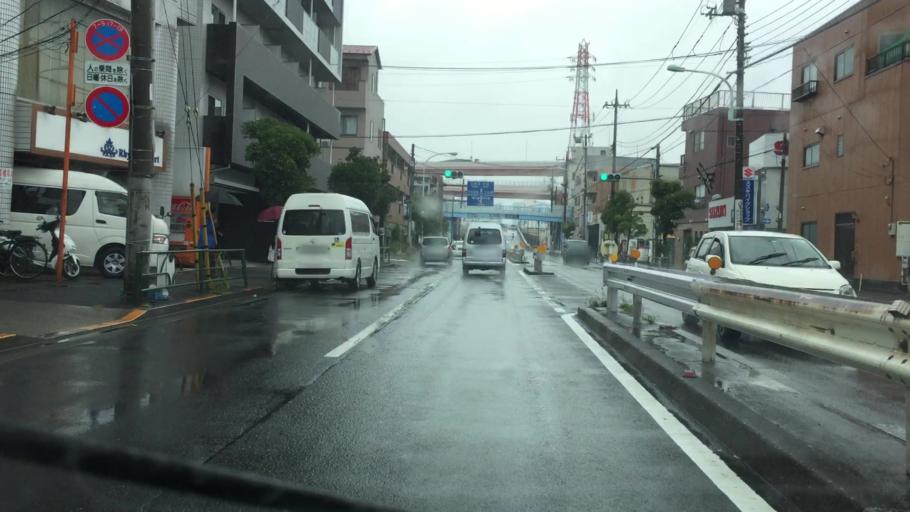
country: JP
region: Saitama
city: Soka
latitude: 35.7636
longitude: 139.7871
